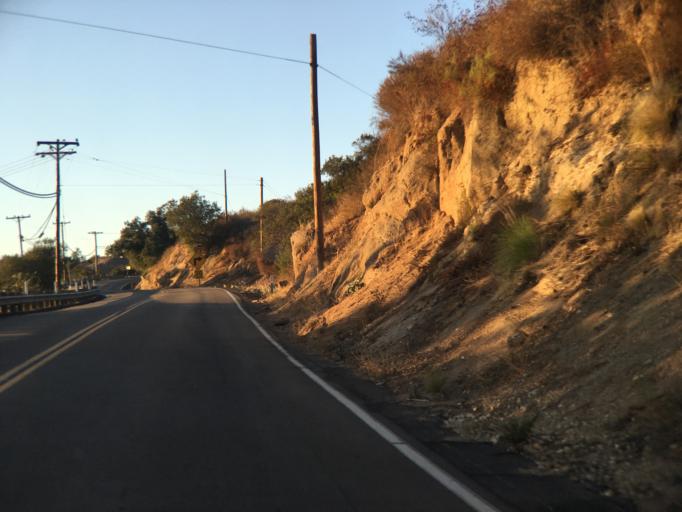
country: US
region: California
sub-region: San Diego County
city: Alpine
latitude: 32.8051
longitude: -116.7792
